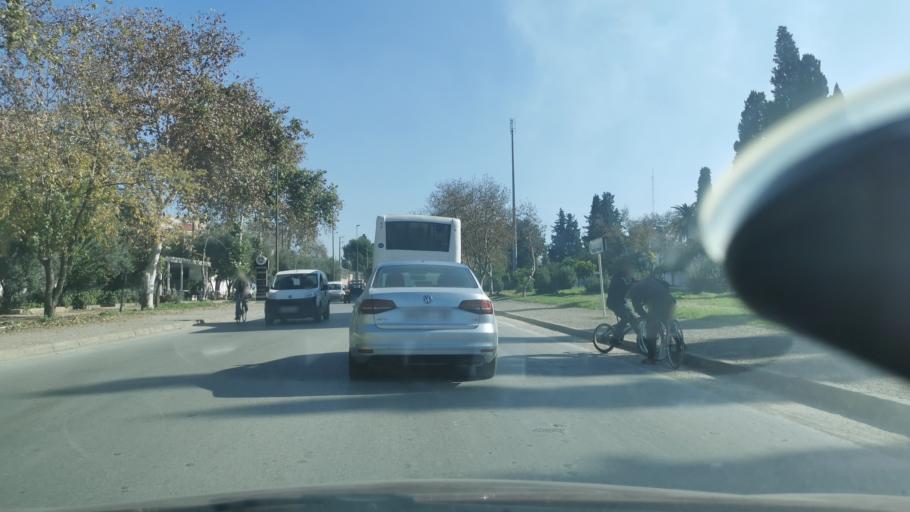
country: MA
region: Fes-Boulemane
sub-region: Fes
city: Fes
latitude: 34.0319
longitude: -4.9870
